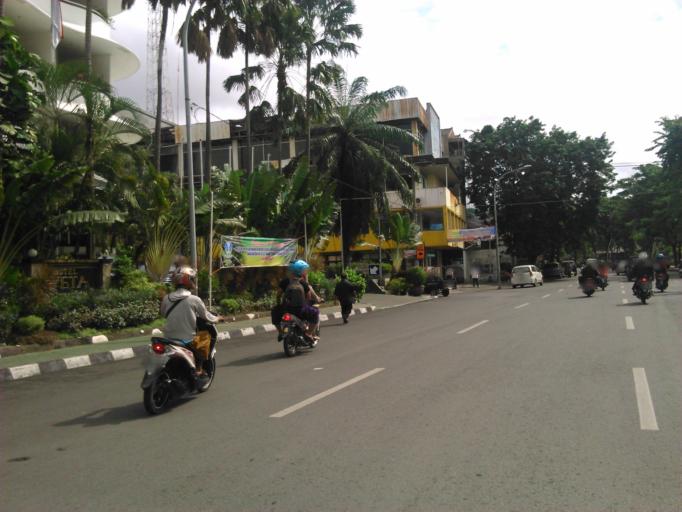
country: ID
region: East Java
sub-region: Kota Surabaya
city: Surabaya
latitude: -7.2590
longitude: 112.7430
